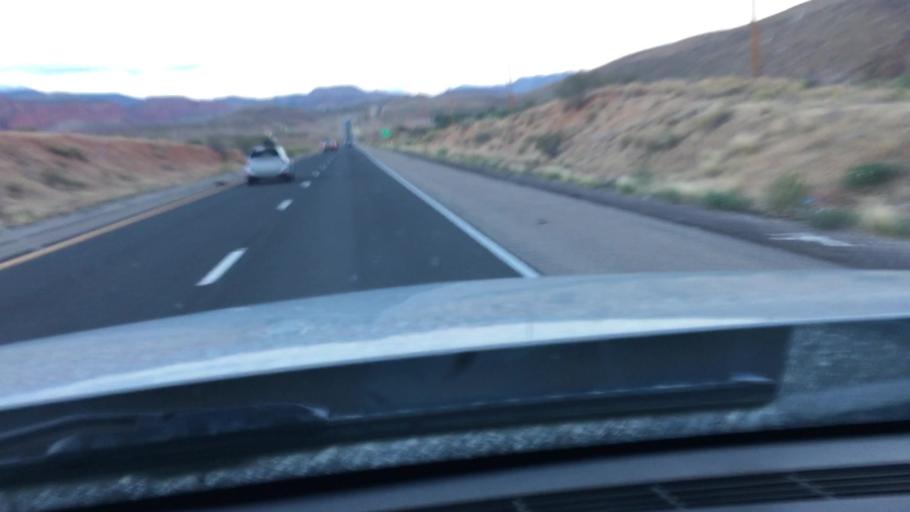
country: US
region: Utah
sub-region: Washington County
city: Hurricane
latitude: 37.1995
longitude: -113.3995
